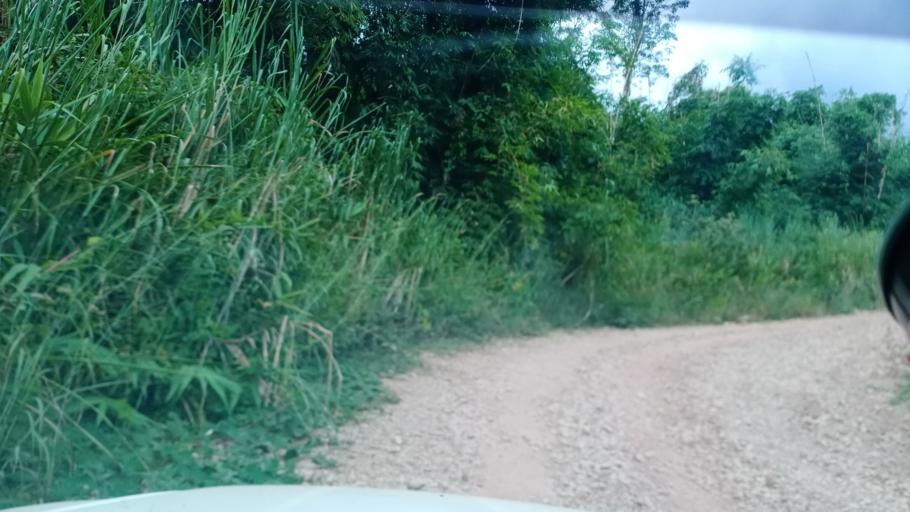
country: TH
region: Changwat Bueng Kan
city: Pak Khat
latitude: 18.7263
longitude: 103.2658
